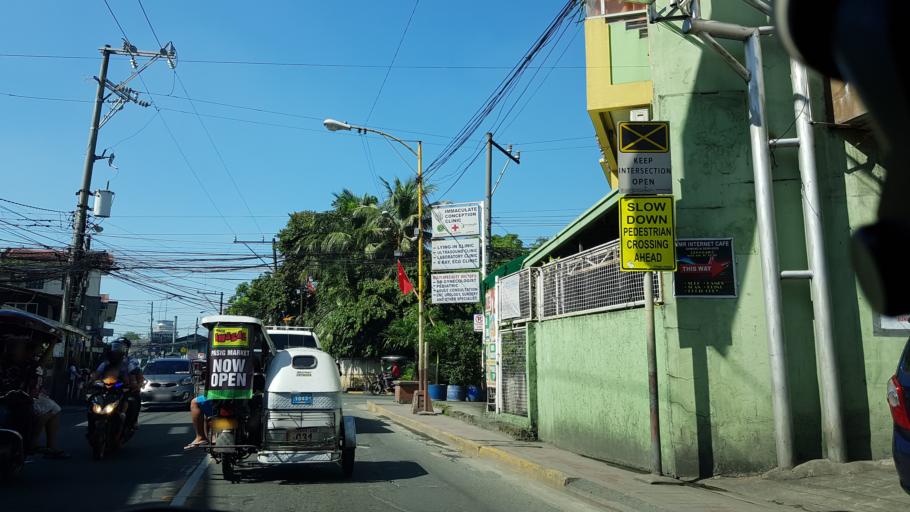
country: PH
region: Calabarzon
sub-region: Province of Rizal
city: Pateros
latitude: 14.5649
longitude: 121.0852
